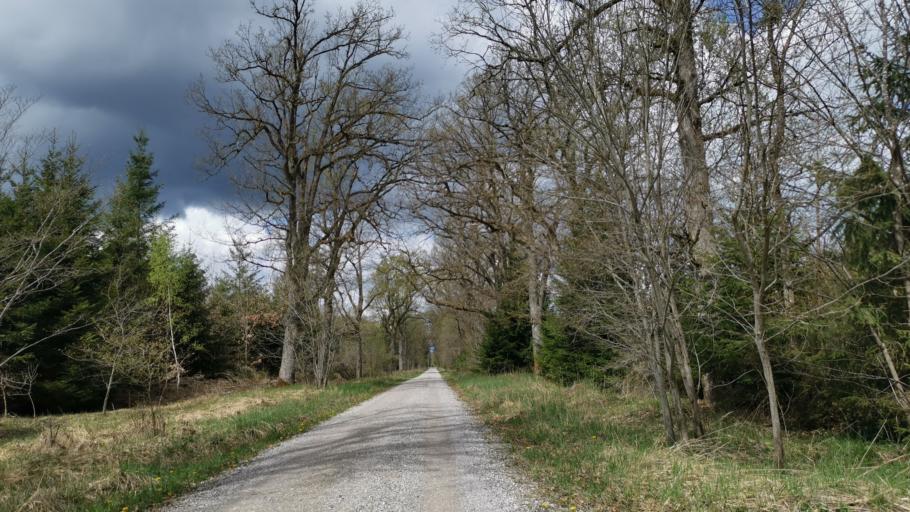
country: DE
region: Bavaria
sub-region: Upper Bavaria
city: Neuried
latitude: 48.0587
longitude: 11.4511
